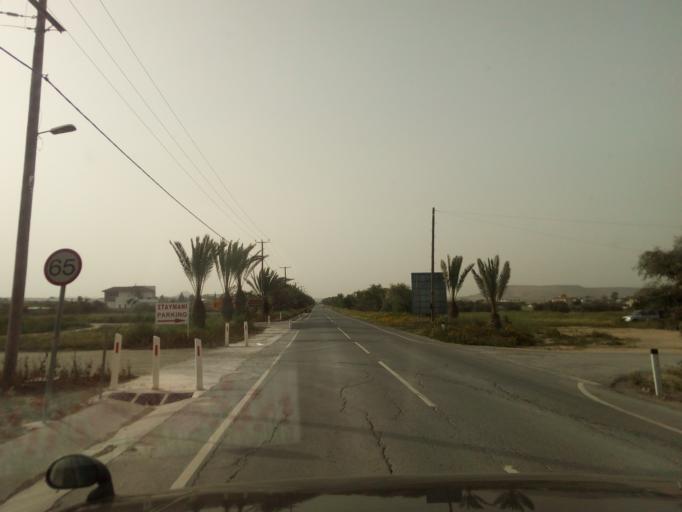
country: CY
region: Larnaka
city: Athienou
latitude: 35.0549
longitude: 33.5317
